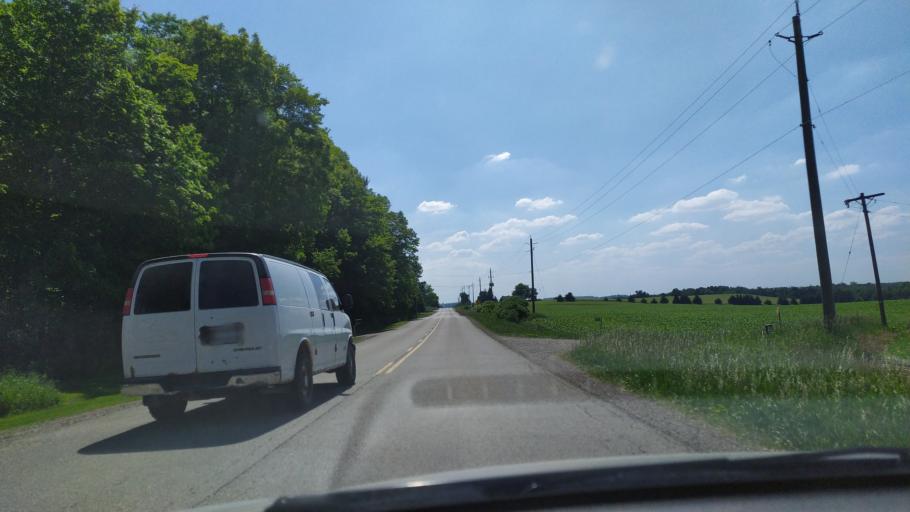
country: CA
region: Ontario
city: Kitchener
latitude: 43.3631
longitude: -80.6121
